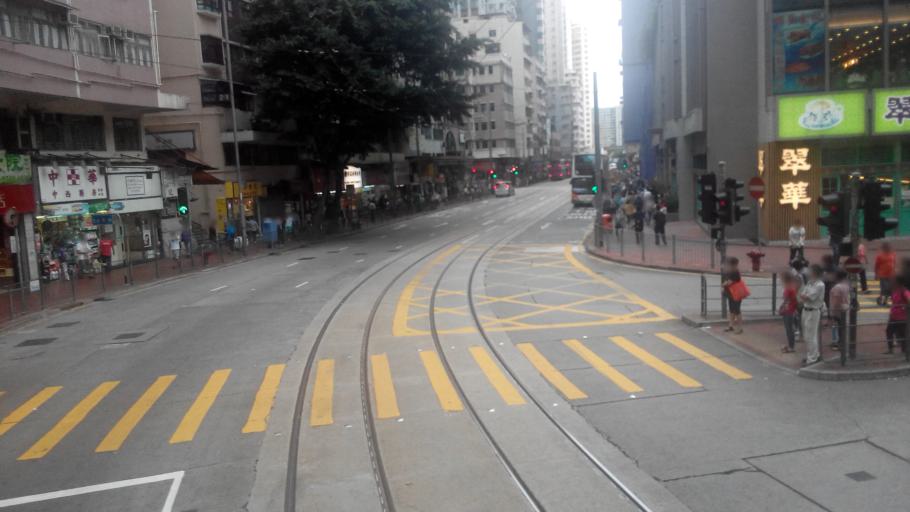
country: HK
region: Wanchai
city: Wan Chai
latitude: 22.2775
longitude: 114.2272
